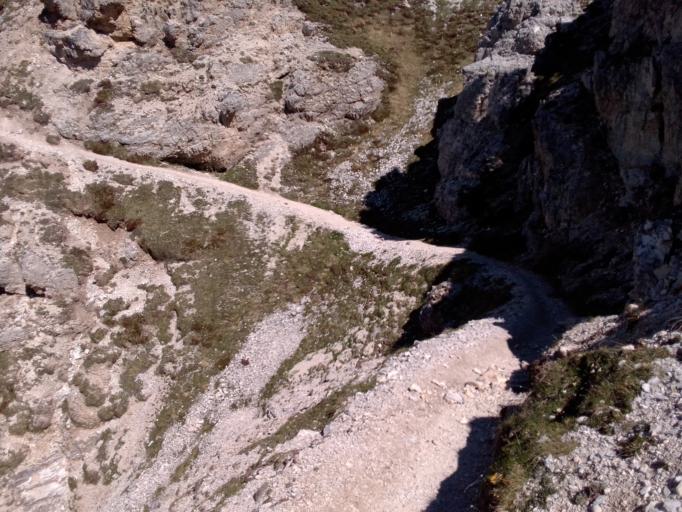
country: IT
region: Trentino-Alto Adige
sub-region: Bolzano
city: Dobbiaco
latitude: 46.6135
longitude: 12.2467
